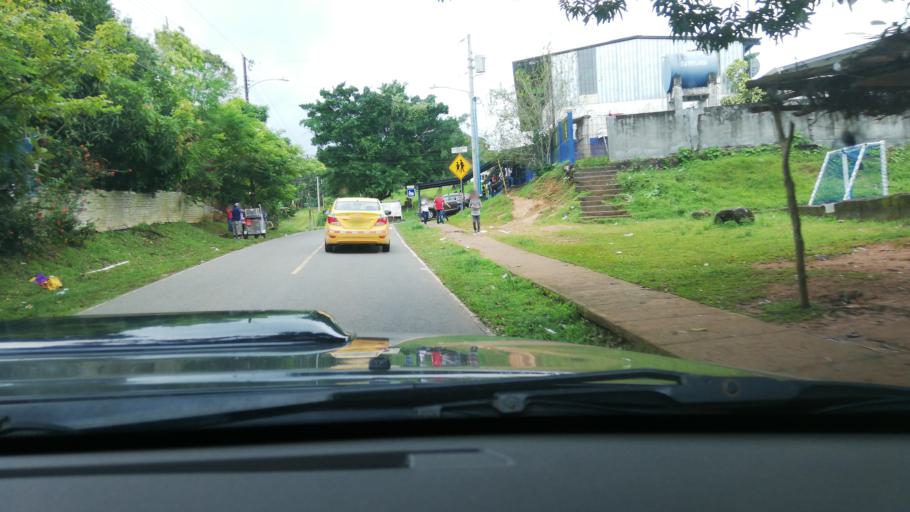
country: PA
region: Panama
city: Cerro Azul
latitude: 9.1103
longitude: -79.4436
